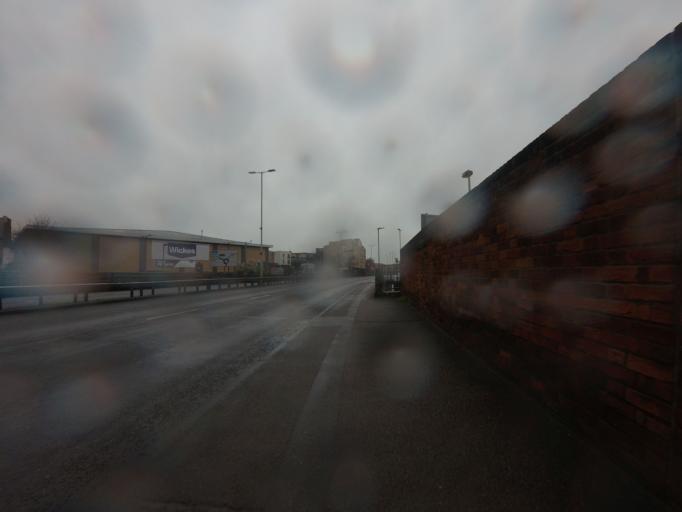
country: GB
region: England
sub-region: Hertfordshire
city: Waltham Cross
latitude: 51.6878
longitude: -0.0326
